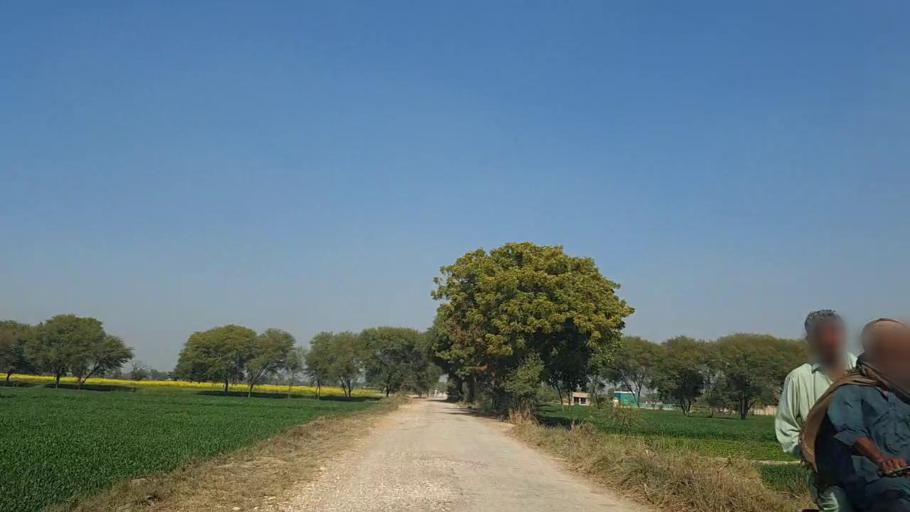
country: PK
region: Sindh
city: Nawabshah
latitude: 26.2312
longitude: 68.3380
